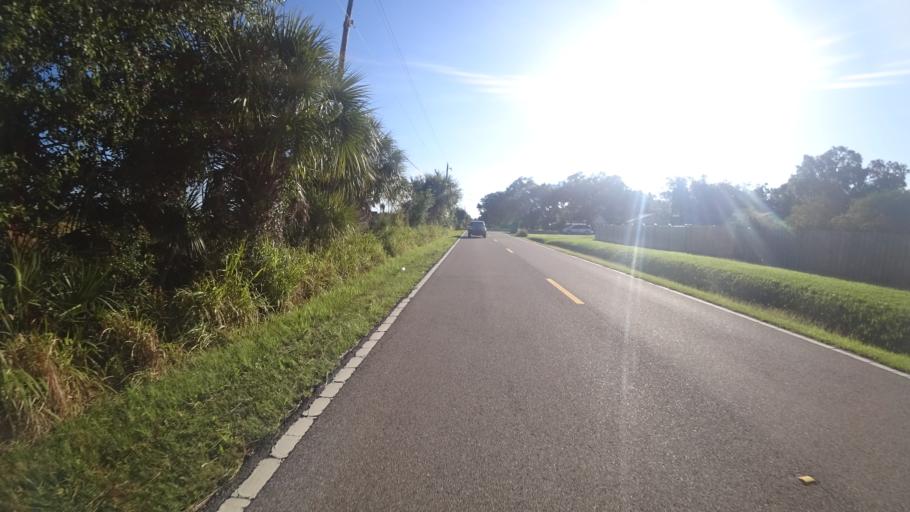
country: US
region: Florida
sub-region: Manatee County
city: Memphis
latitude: 27.5682
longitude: -82.5408
